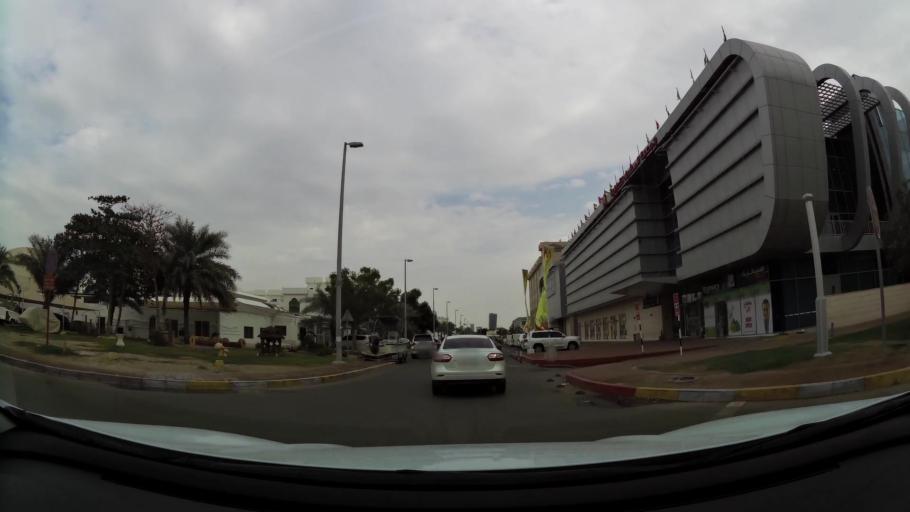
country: AE
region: Abu Dhabi
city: Abu Dhabi
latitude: 24.4267
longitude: 54.4072
